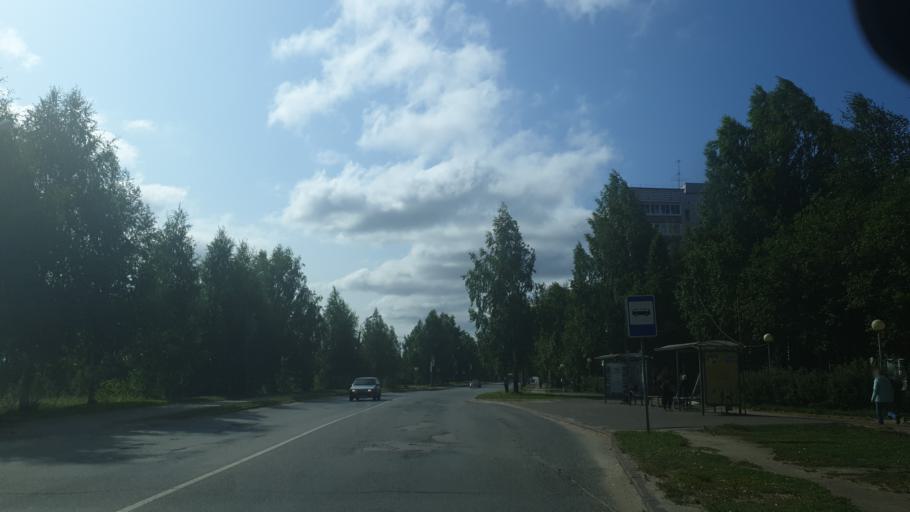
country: RU
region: Komi Republic
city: Ezhva
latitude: 61.7952
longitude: 50.7510
